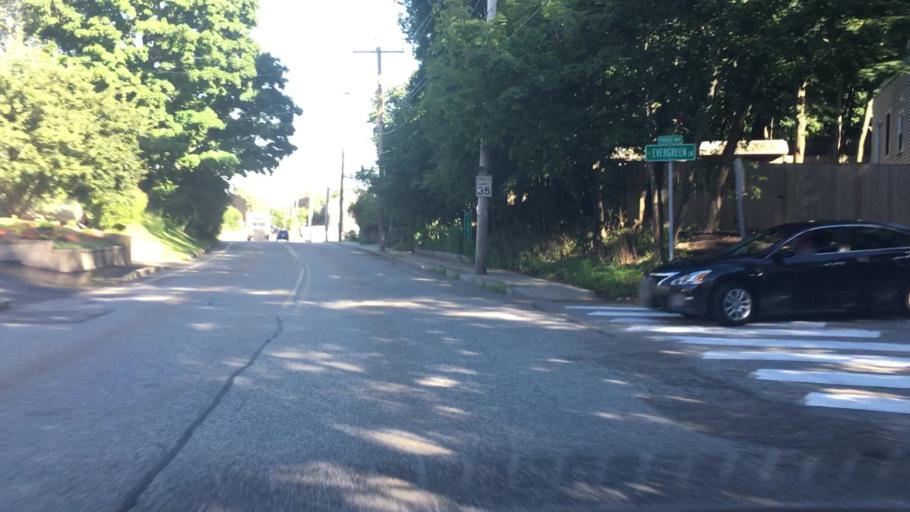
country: US
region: Massachusetts
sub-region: Middlesex County
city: Arlington
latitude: 42.4331
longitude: -71.1844
